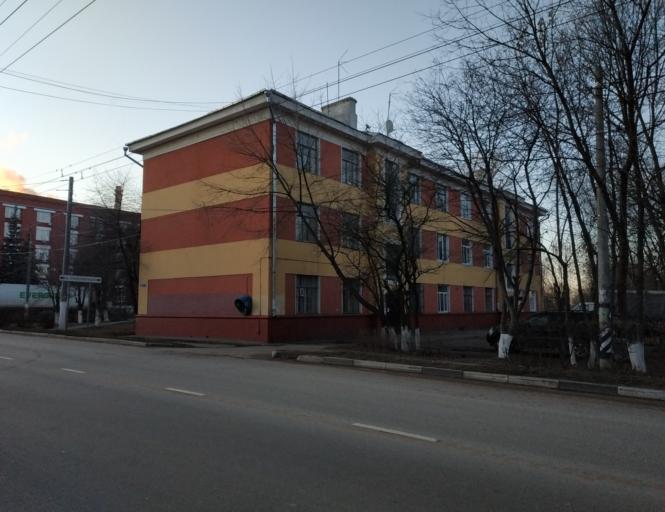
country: RU
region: Moskovskaya
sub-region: Podol'skiy Rayon
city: Podol'sk
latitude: 55.4190
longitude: 37.5730
